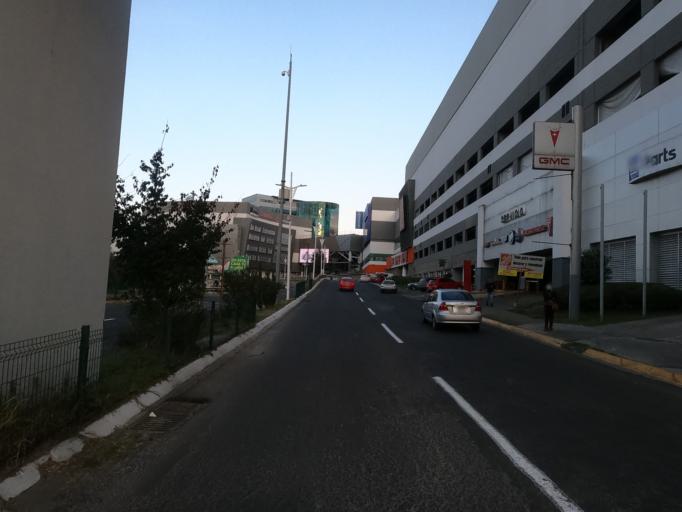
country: MX
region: Mexico
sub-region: Huixquilucan
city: Naucalpan de Juarez
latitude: 19.4060
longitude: -99.2743
